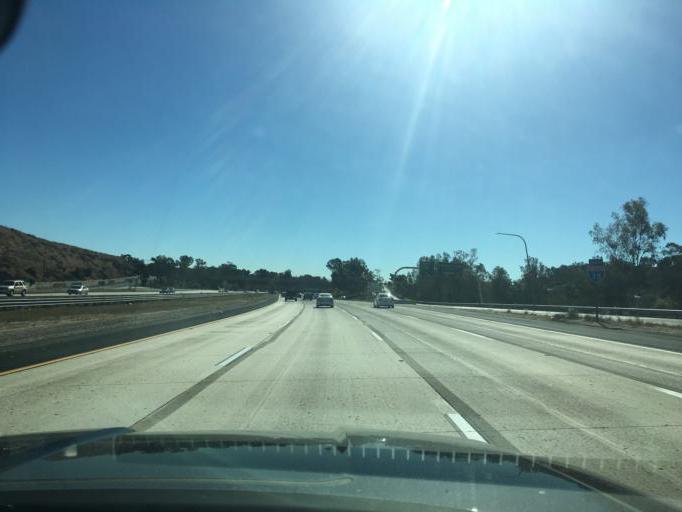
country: US
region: California
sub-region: San Diego County
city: La Mesa
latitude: 32.8375
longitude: -117.1208
